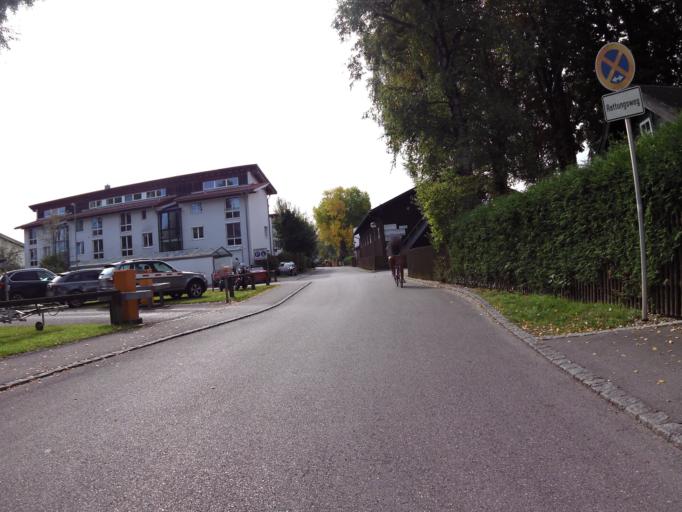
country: DE
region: Bavaria
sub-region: Upper Bavaria
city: Starnberg
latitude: 47.9997
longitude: 11.3577
